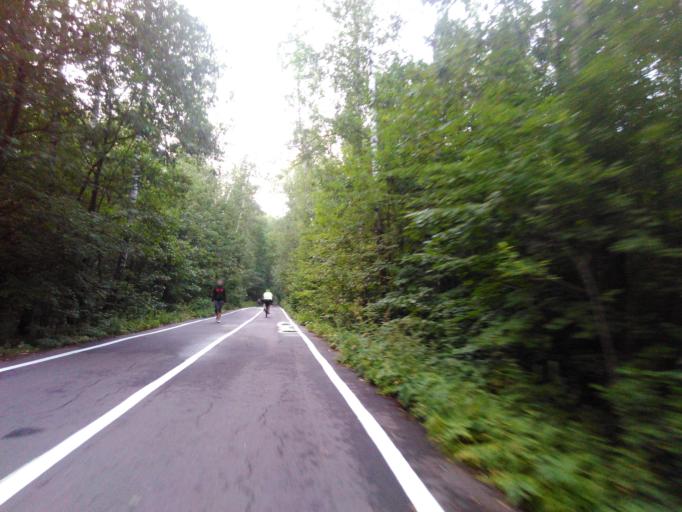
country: RU
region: Moscow
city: Babushkin
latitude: 55.8504
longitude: 37.7257
